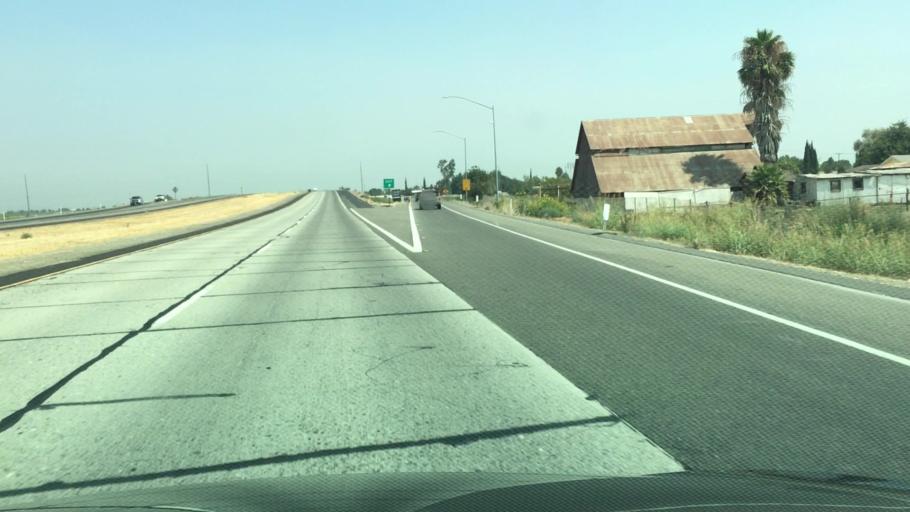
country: US
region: California
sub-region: Merced County
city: Dos Palos
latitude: 37.0521
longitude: -120.6409
